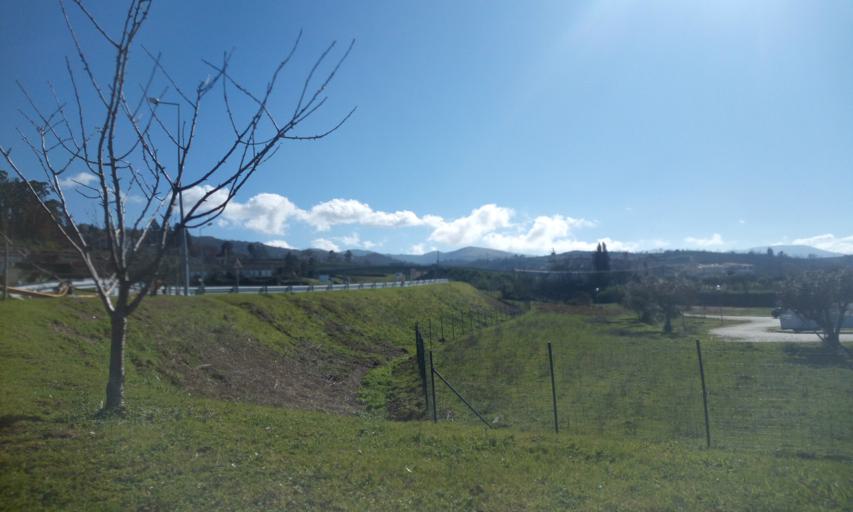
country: PT
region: Guarda
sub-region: Manteigas
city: Manteigas
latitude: 40.4928
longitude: -7.6009
